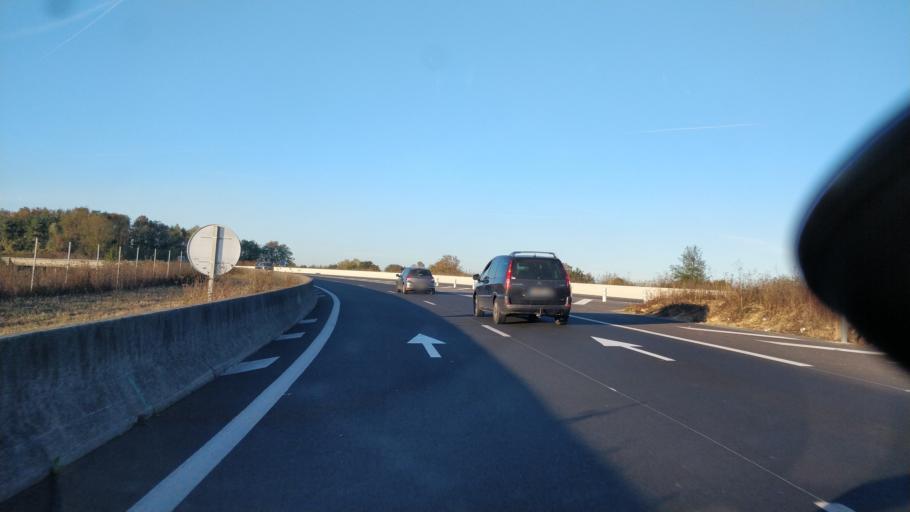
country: FR
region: Ile-de-France
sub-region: Departement de Seine-et-Marne
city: Bailly-Romainvilliers
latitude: 48.8392
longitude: 2.8222
